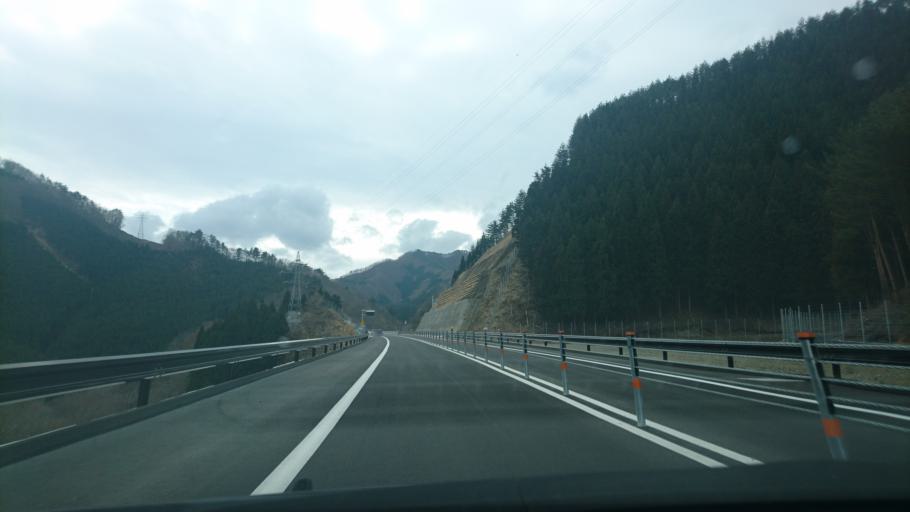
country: JP
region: Iwate
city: Kamaishi
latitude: 39.2979
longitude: 141.8678
